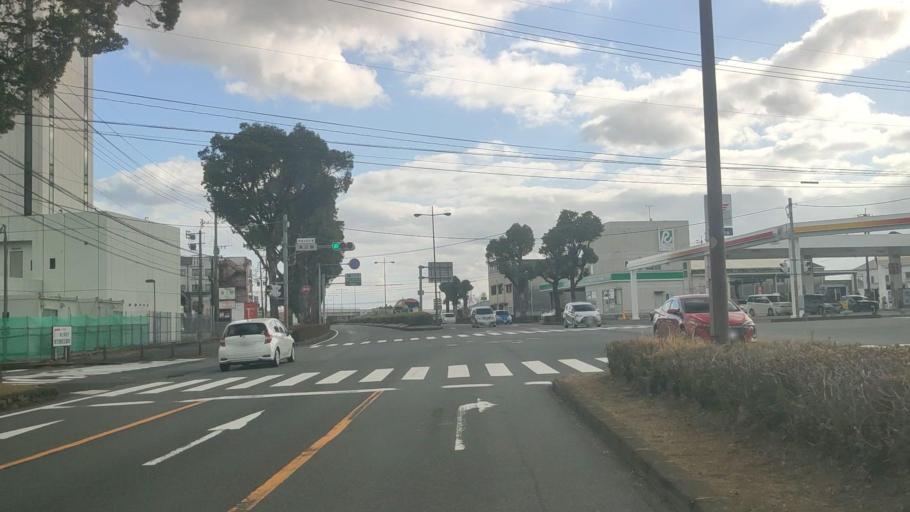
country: JP
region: Kagoshima
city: Kokubu-matsuki
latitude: 31.7953
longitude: 130.7183
